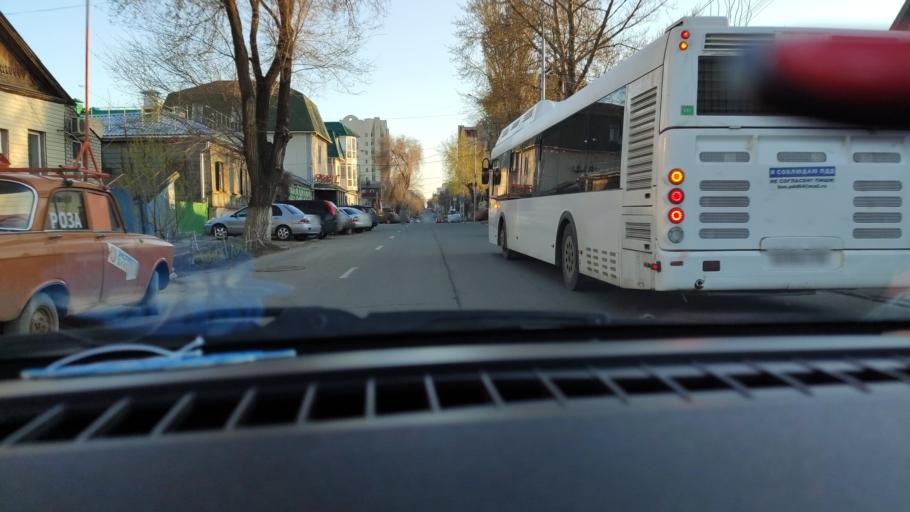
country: RU
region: Saratov
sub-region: Saratovskiy Rayon
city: Saratov
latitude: 51.5422
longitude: 46.0313
